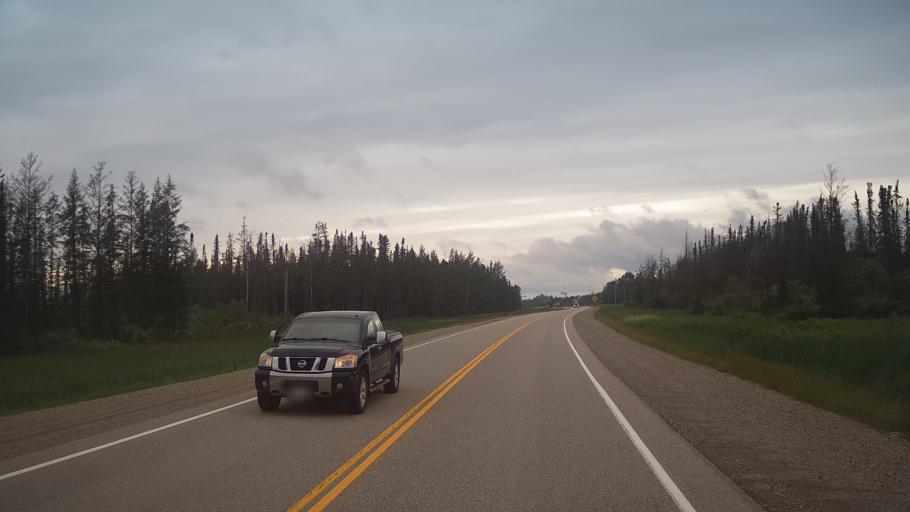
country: CA
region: Ontario
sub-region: Thunder Bay District
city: Thunder Bay
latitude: 48.8888
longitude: -90.0049
